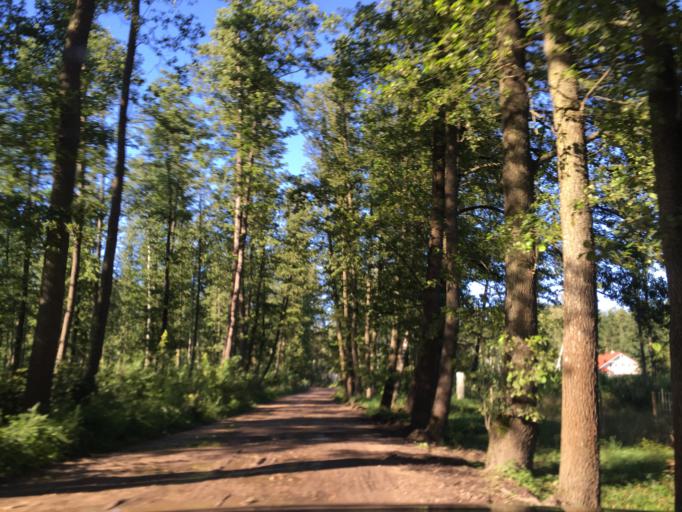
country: LV
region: Riga
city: Jaunciems
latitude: 57.0636
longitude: 24.1363
